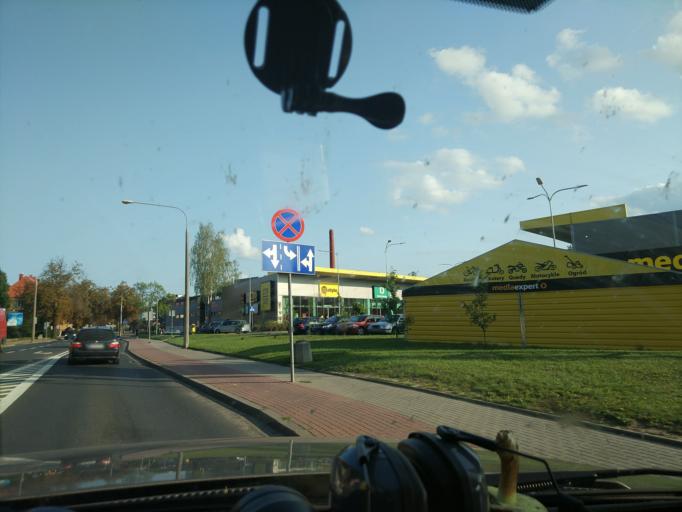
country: PL
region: Warmian-Masurian Voivodeship
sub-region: Powiat szczycienski
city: Szczytno
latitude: 53.5635
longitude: 20.9875
